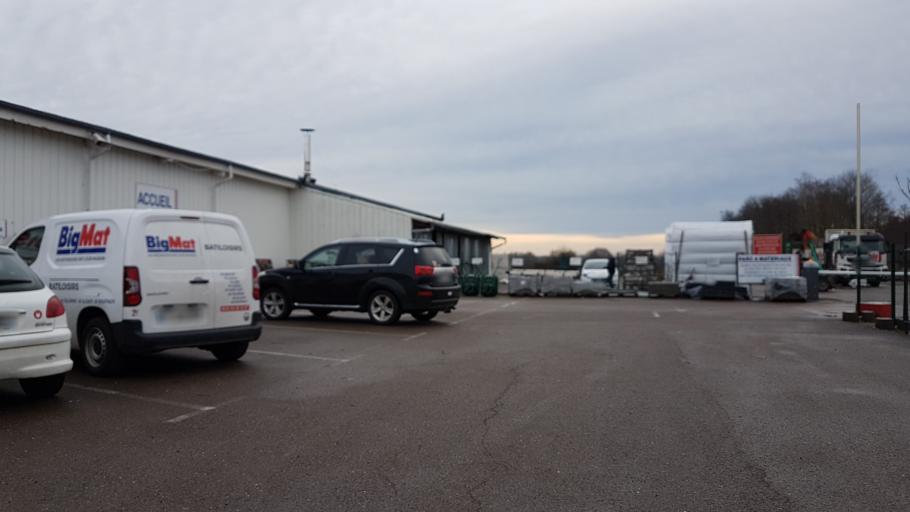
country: FR
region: Franche-Comte
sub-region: Departement de la Haute-Saone
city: Luxeuil-les-Bains
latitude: 47.8075
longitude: 6.3699
